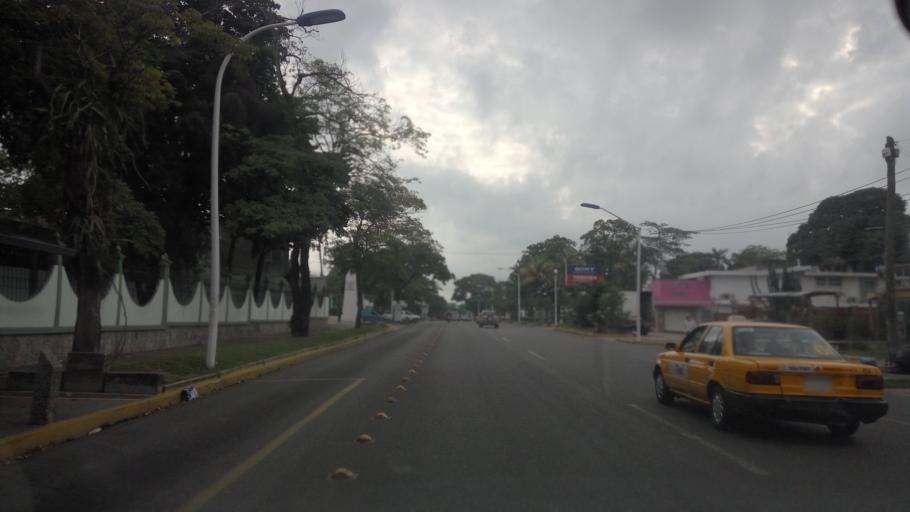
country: MX
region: Tabasco
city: Villahermosa
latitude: 17.9828
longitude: -92.9403
